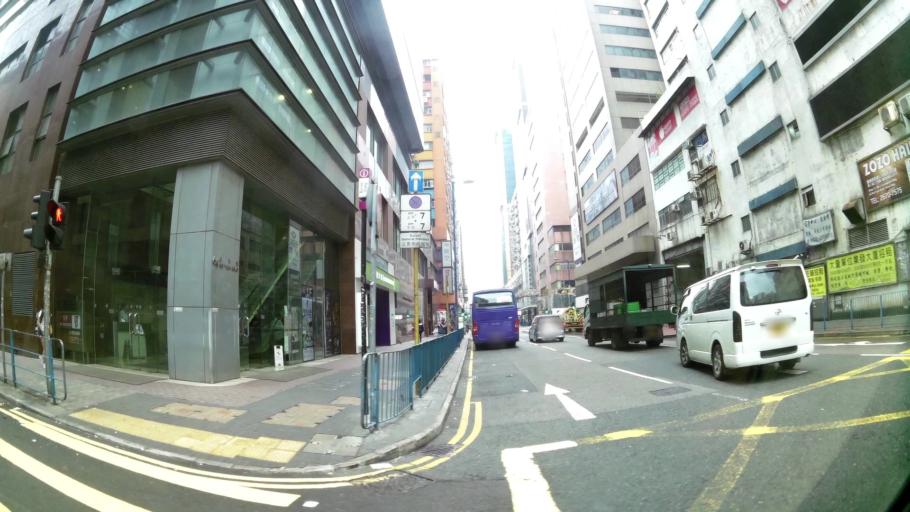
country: HK
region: Kowloon City
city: Kowloon
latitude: 22.3111
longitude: 114.2255
